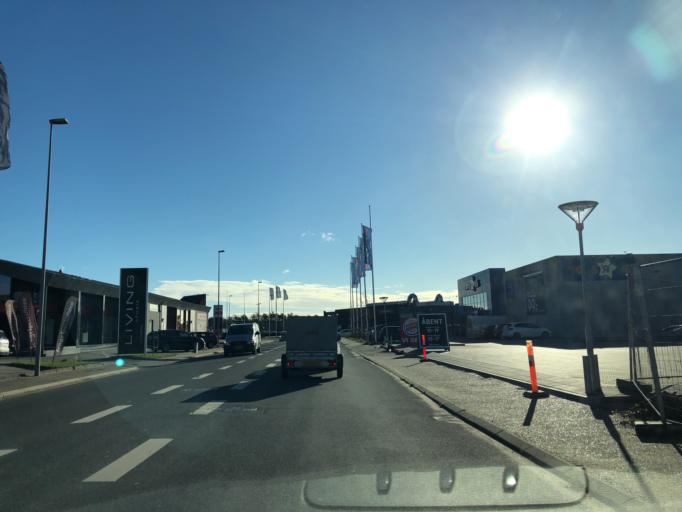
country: DK
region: Central Jutland
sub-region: Holstebro Kommune
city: Holstebro
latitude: 56.3779
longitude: 8.6192
